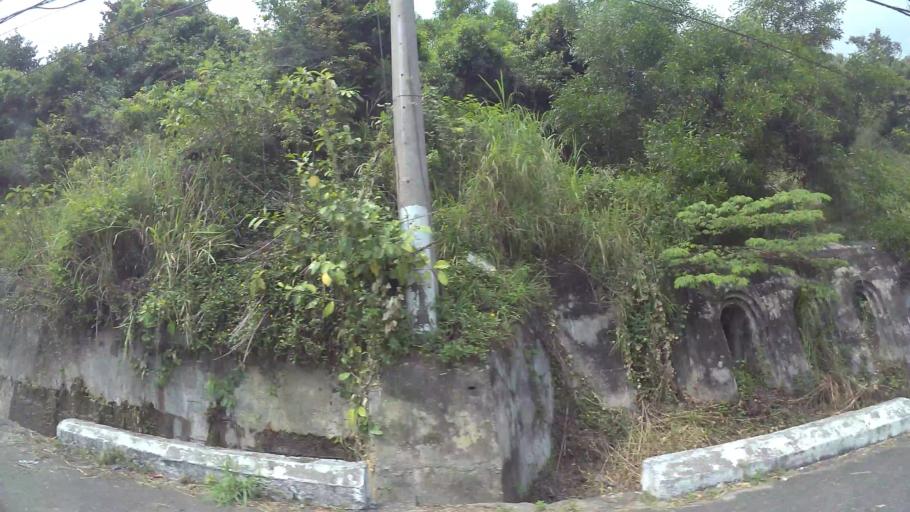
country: VN
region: Da Nang
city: Son Tra
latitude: 16.1039
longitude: 108.2835
